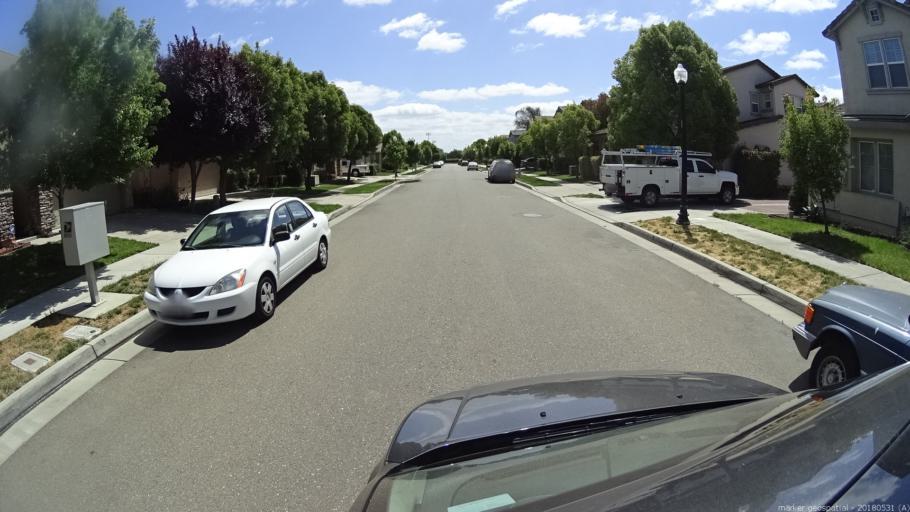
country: US
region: California
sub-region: Sacramento County
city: Sacramento
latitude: 38.6314
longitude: -121.5014
